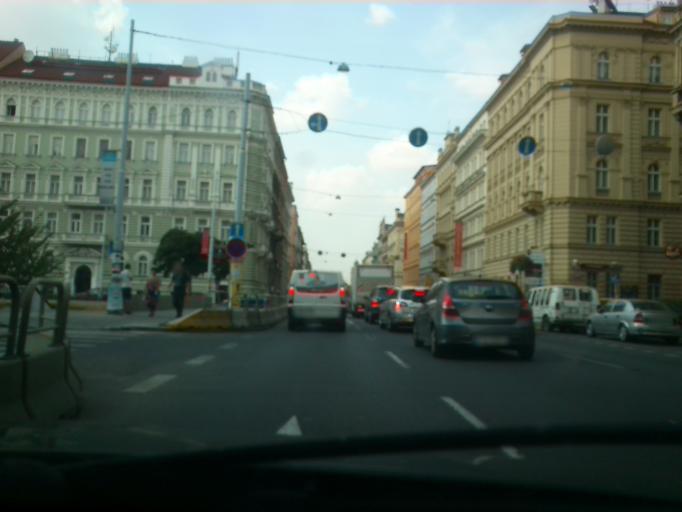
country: CZ
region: Praha
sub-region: Praha 2
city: Vysehrad
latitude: 50.0715
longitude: 14.4306
